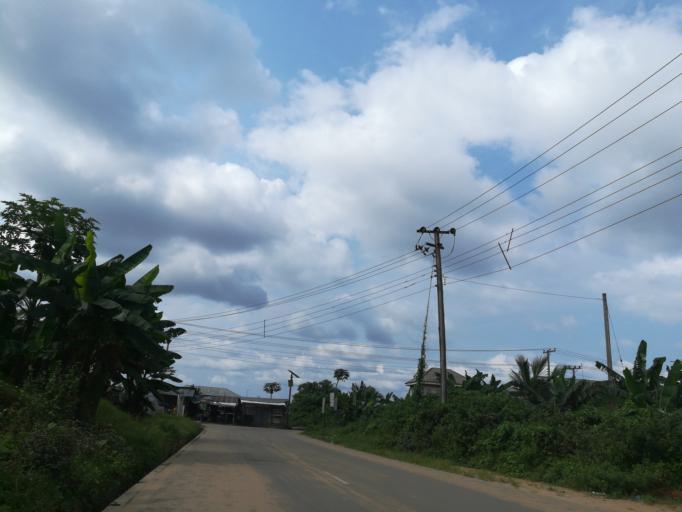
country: NG
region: Rivers
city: Okrika
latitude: 4.7454
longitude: 7.1129
